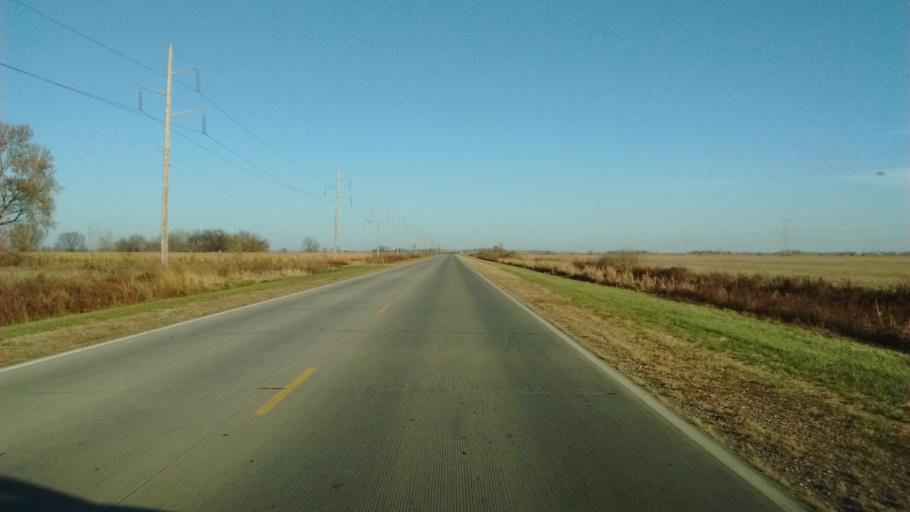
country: US
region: Iowa
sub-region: Woodbury County
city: Sergeant Bluff
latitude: 42.3302
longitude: -96.3383
